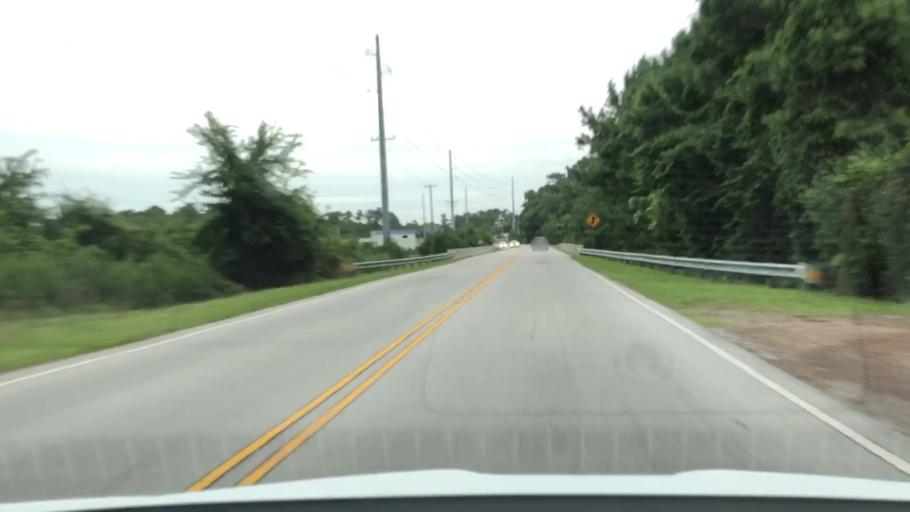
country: US
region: North Carolina
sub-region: Carteret County
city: Cape Carteret
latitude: 34.7104
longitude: -77.0680
